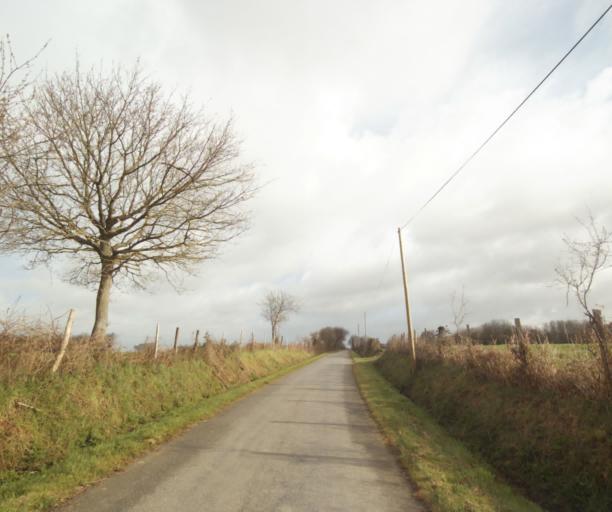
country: FR
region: Pays de la Loire
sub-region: Departement de la Loire-Atlantique
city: Bouvron
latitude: 47.3966
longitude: -1.8613
